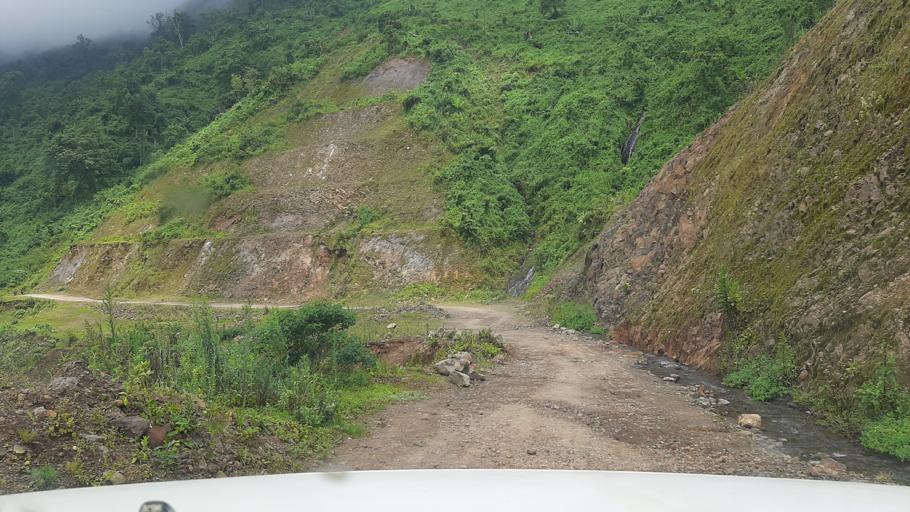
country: ET
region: Southern Nations, Nationalities, and People's Region
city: Bonga
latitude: 7.1330
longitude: 36.5586
